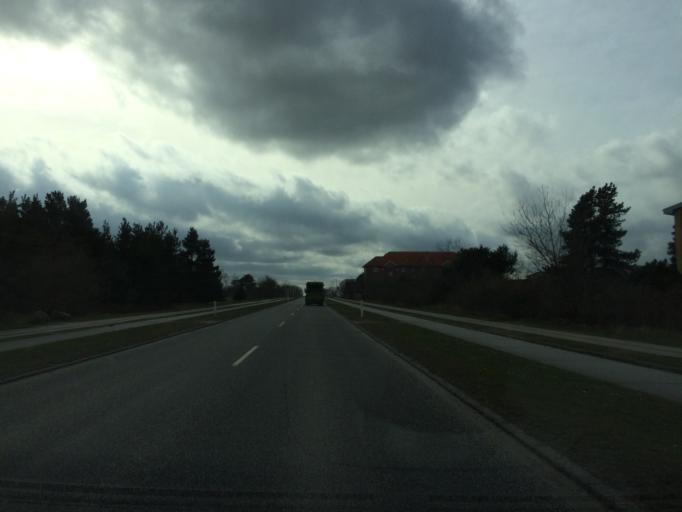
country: DK
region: Central Jutland
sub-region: Norddjurs Kommune
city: Grenaa
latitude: 56.4062
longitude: 10.8816
